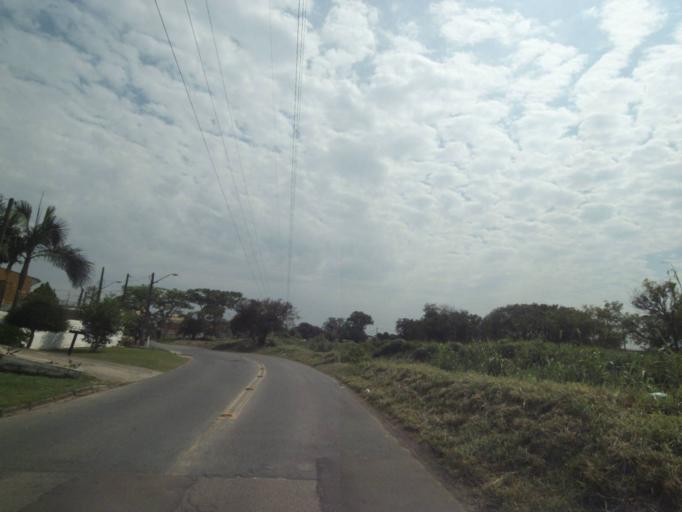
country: BR
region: Parana
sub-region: Pinhais
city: Pinhais
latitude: -25.4187
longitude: -49.1983
